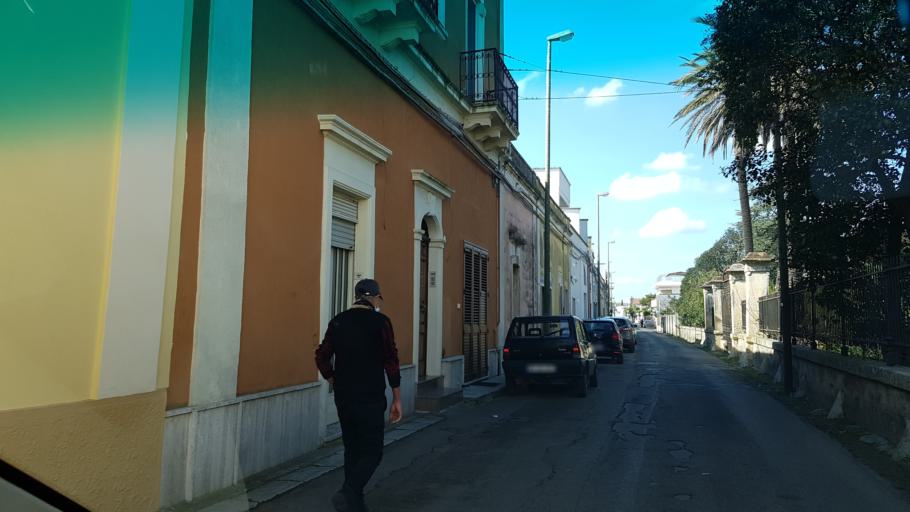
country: IT
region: Apulia
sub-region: Provincia di Lecce
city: Veglie
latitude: 40.3360
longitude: 17.9684
